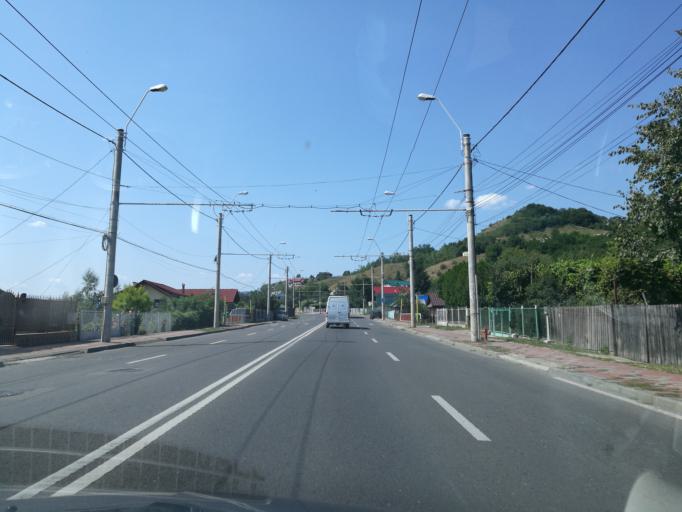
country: RO
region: Neamt
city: Piatra Neamt
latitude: 46.9403
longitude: 26.3303
